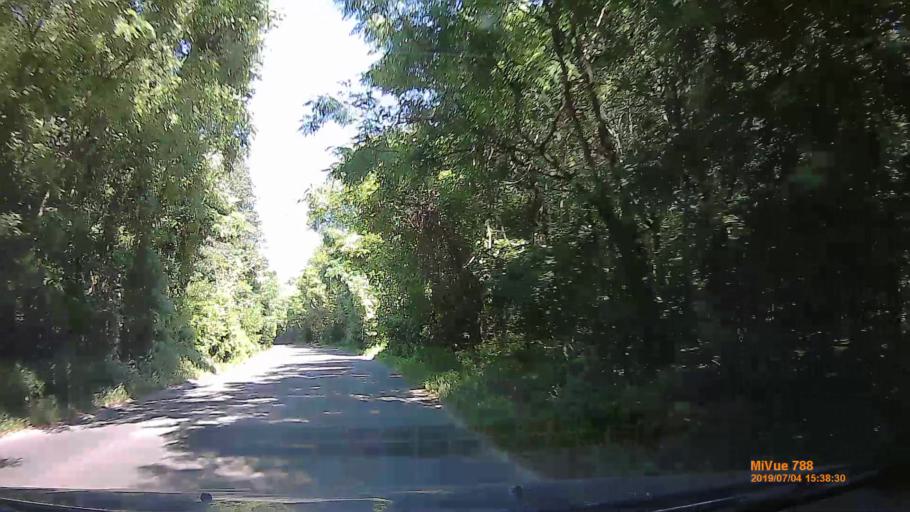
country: HU
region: Komarom-Esztergom
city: Tatabanya
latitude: 47.5543
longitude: 18.3964
